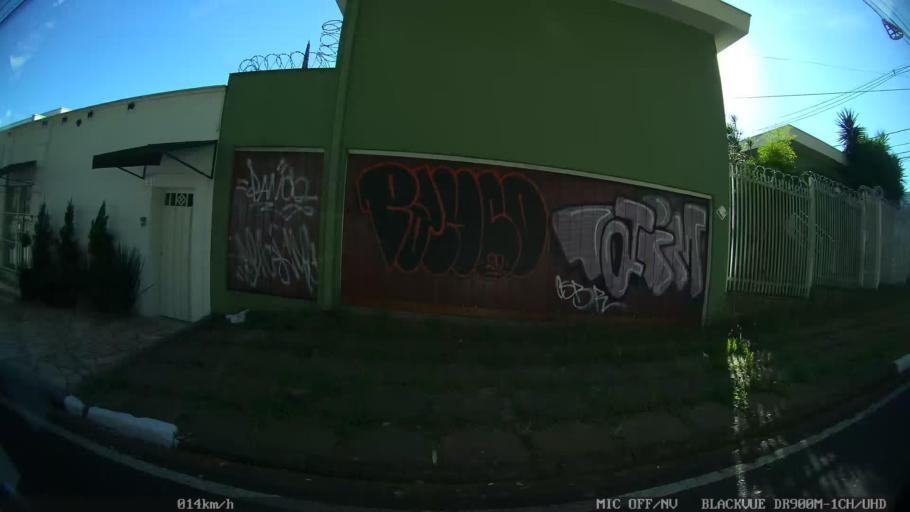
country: BR
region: Sao Paulo
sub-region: Franca
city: Franca
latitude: -20.5417
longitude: -47.4042
